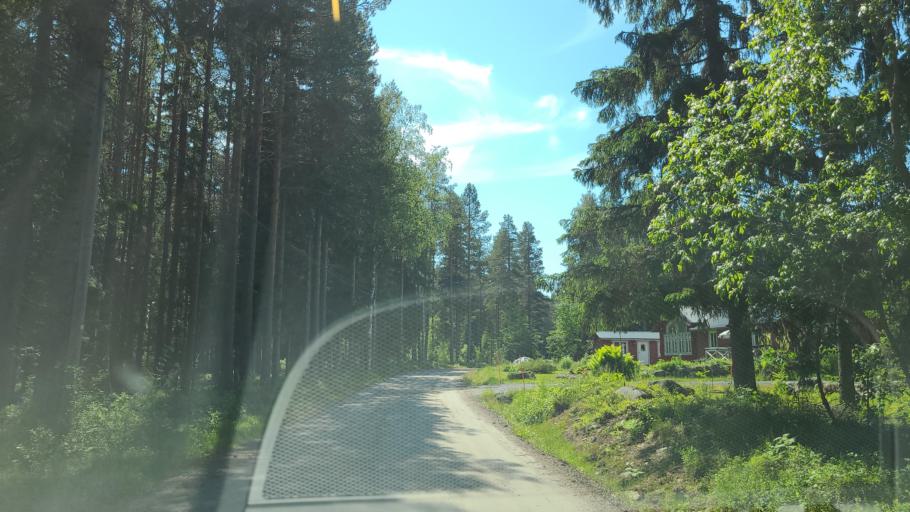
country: SE
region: Vaesterbotten
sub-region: Robertsfors Kommun
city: Robertsfors
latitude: 64.1439
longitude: 20.9608
